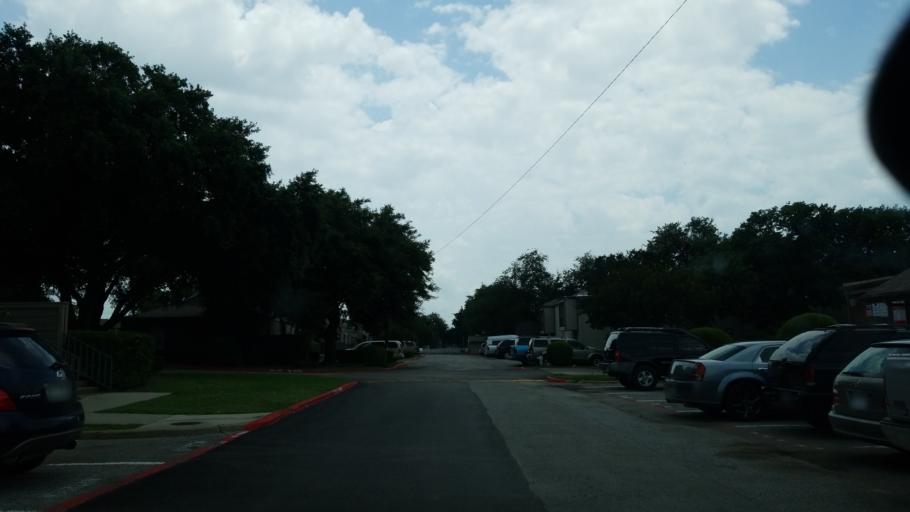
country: US
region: Texas
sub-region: Dallas County
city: Farmers Branch
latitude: 32.8737
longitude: -96.8652
